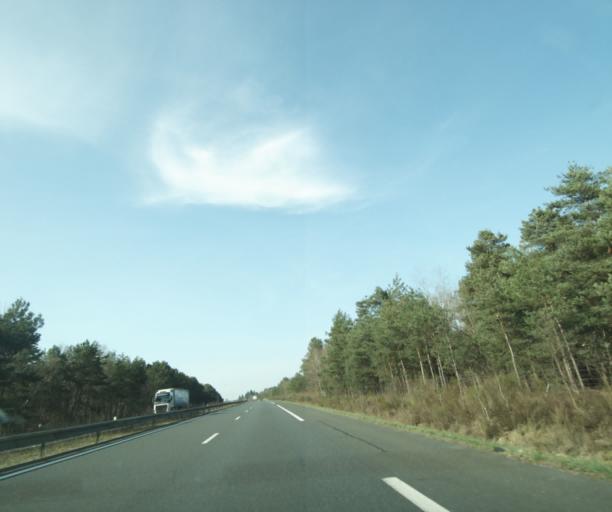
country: FR
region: Centre
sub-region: Departement du Loir-et-Cher
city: Chaumont-sur-Tharonne
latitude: 47.6216
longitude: 1.9615
